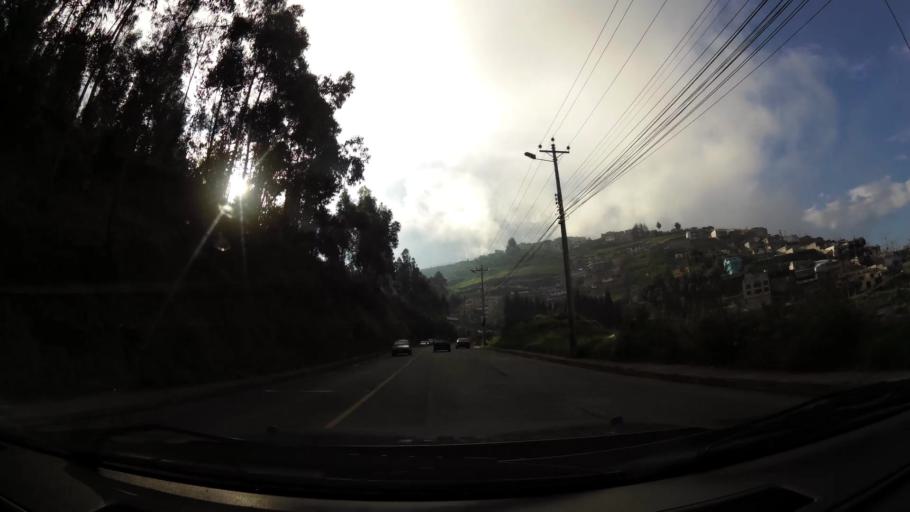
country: EC
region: Pichincha
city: Quito
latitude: -0.2559
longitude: -78.4970
